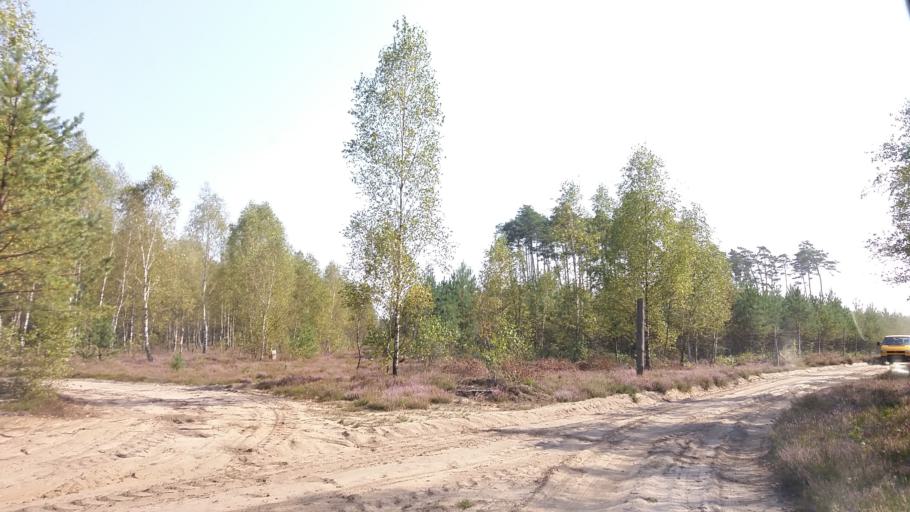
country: PL
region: West Pomeranian Voivodeship
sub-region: Powiat drawski
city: Kalisz Pomorski
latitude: 53.1367
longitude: 15.9420
